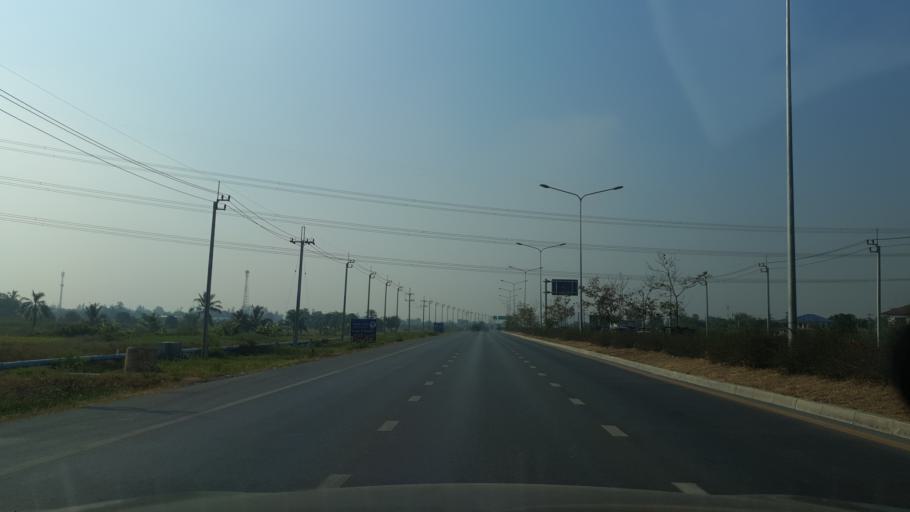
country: TH
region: Nonthaburi
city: Bang Bua Thong
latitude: 13.9711
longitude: 100.4636
